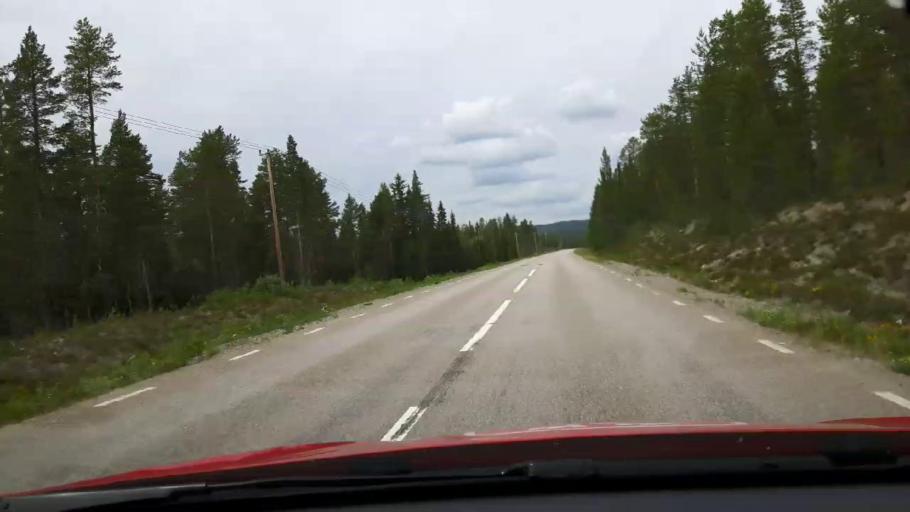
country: SE
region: Jaemtland
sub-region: Harjedalens Kommun
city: Sveg
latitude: 62.3980
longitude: 13.7469
